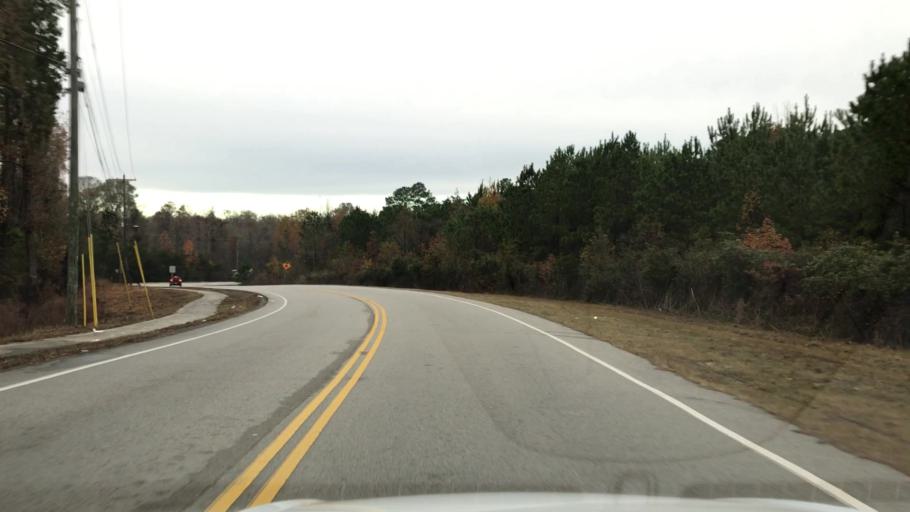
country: US
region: South Carolina
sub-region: Berkeley County
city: Ladson
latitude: 32.9784
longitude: -80.0797
